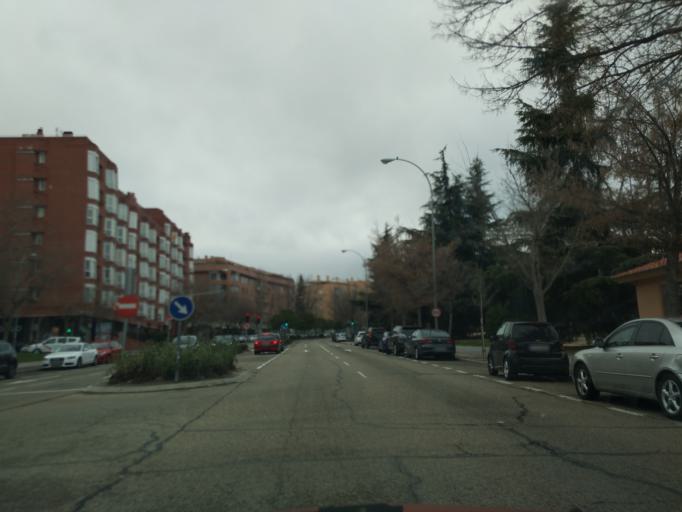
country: ES
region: Madrid
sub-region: Provincia de Madrid
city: Hortaleza
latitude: 40.4609
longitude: -3.6317
